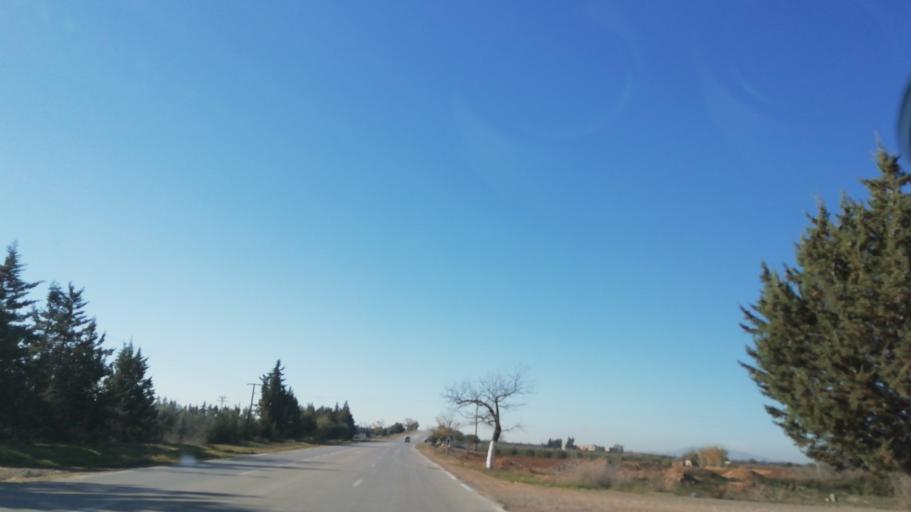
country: MA
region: Oriental
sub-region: Oujda-Angad
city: Oujda
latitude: 34.8110
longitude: -1.8137
